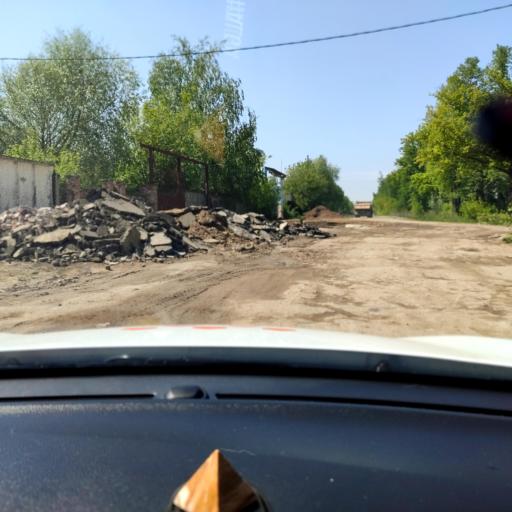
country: RU
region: Tatarstan
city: Stolbishchi
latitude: 55.7111
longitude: 49.1901
